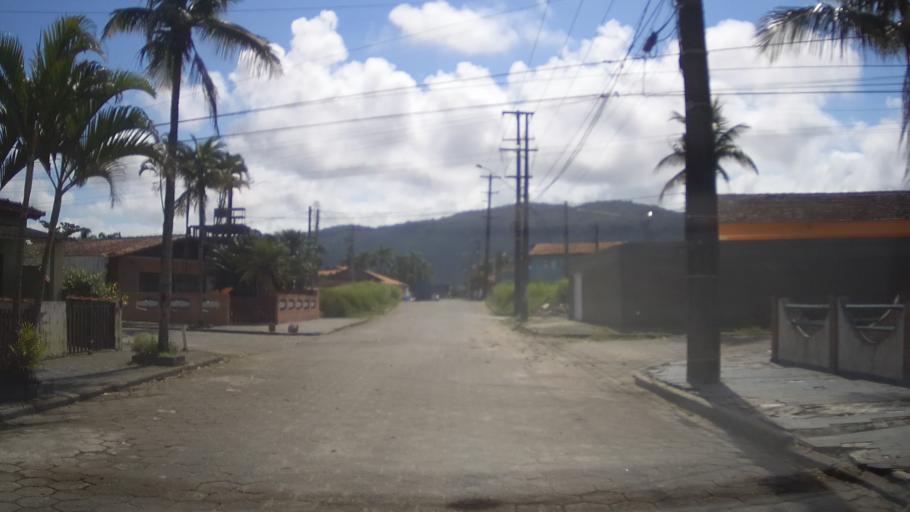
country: BR
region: Sao Paulo
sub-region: Itanhaem
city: Itanhaem
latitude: -24.1488
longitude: -46.7240
